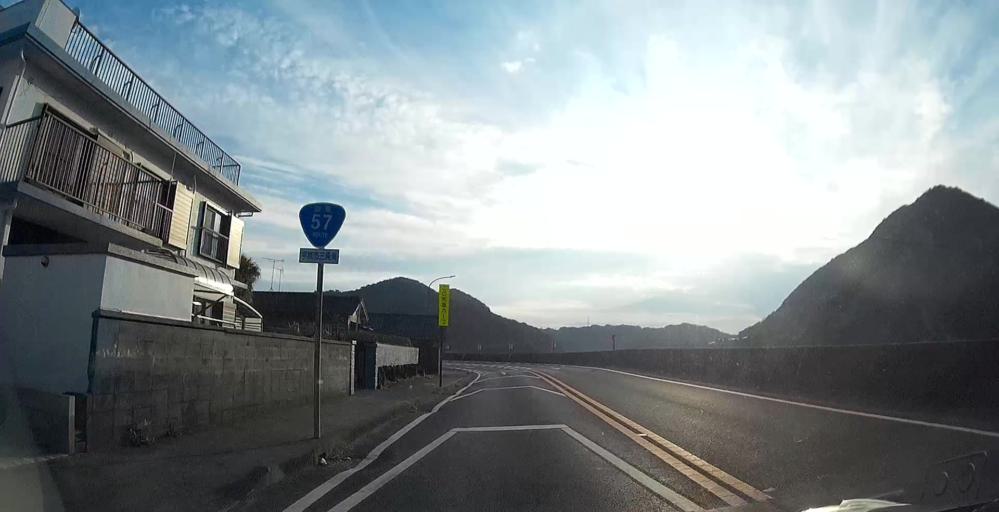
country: JP
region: Nagasaki
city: Shimabara
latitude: 32.6245
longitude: 130.4514
